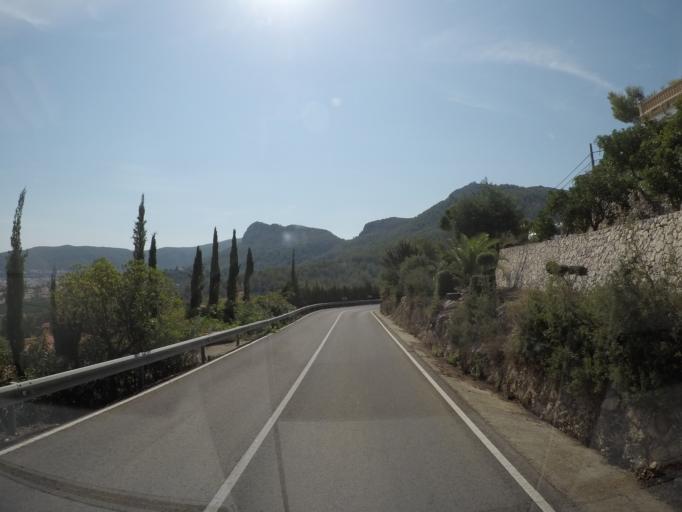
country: ES
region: Valencia
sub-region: Provincia de Alicante
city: Orba
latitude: 38.7835
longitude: -0.0803
